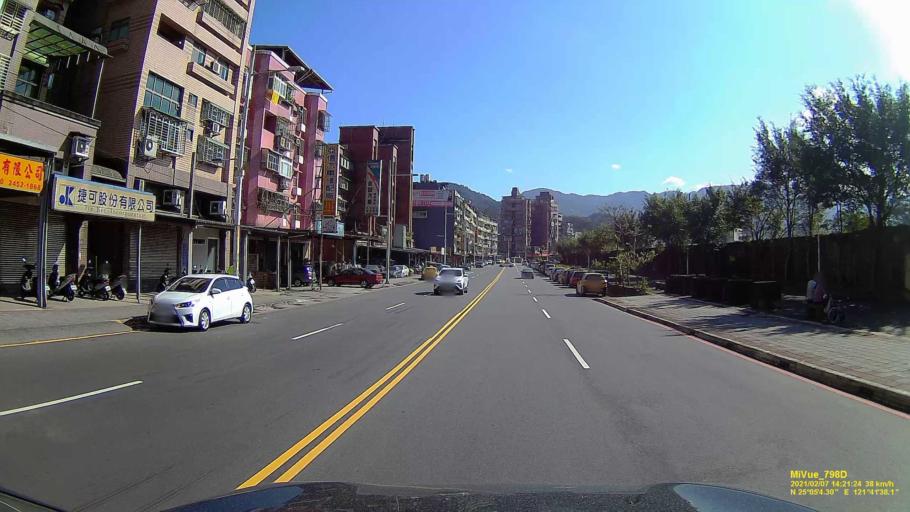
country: TW
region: Taiwan
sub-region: Keelung
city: Keelung
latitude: 25.0844
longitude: 121.6939
